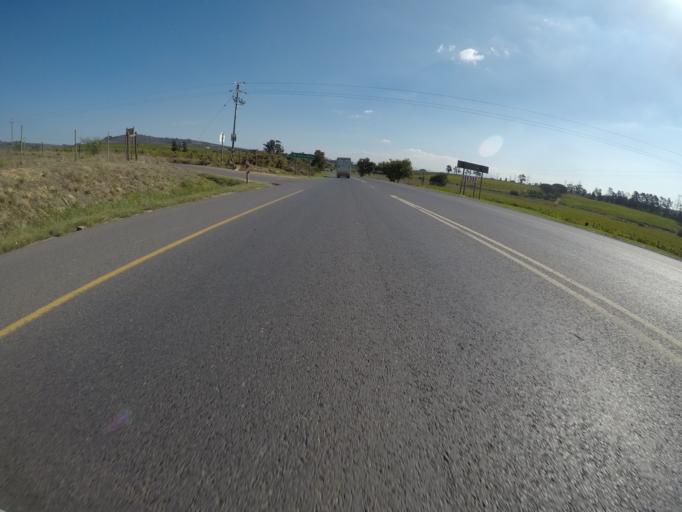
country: ZA
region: Western Cape
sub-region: City of Cape Town
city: Kraaifontein
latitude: -33.8936
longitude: 18.7373
